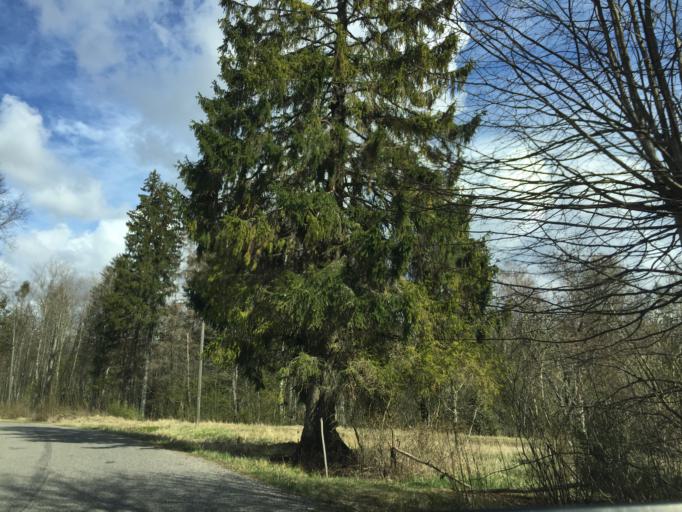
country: LV
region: Limbazu Rajons
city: Limbazi
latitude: 57.6135
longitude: 24.6852
